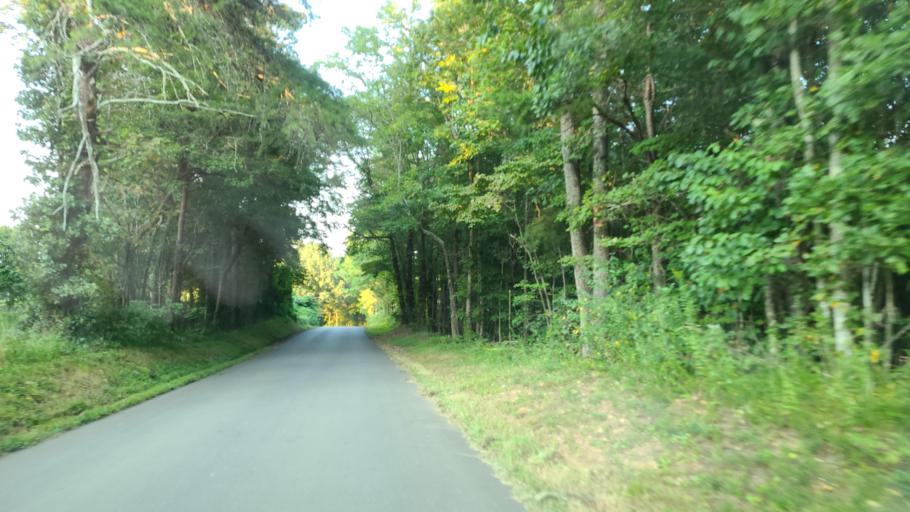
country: US
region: Georgia
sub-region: Pickens County
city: Jasper
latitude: 34.4392
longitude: -84.5616
